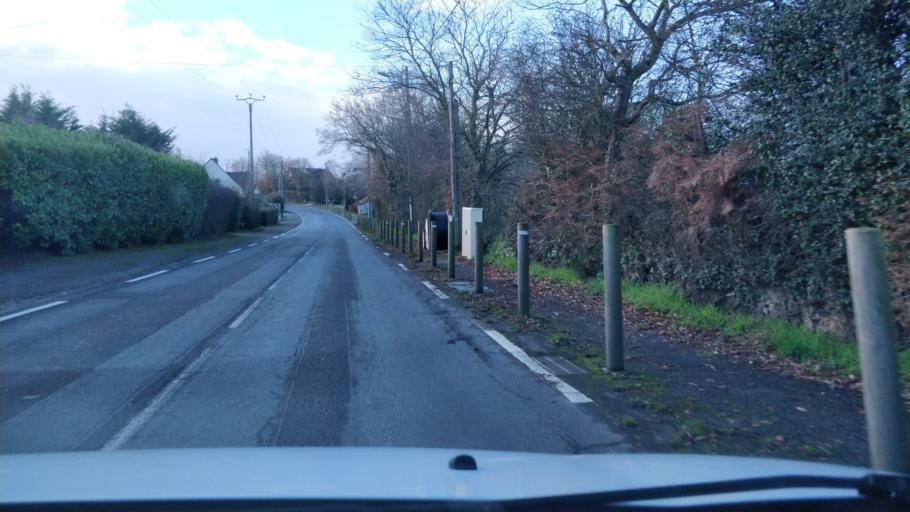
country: FR
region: Pays de la Loire
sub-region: Departement de la Loire-Atlantique
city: Asserac
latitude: 47.4243
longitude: -2.3950
